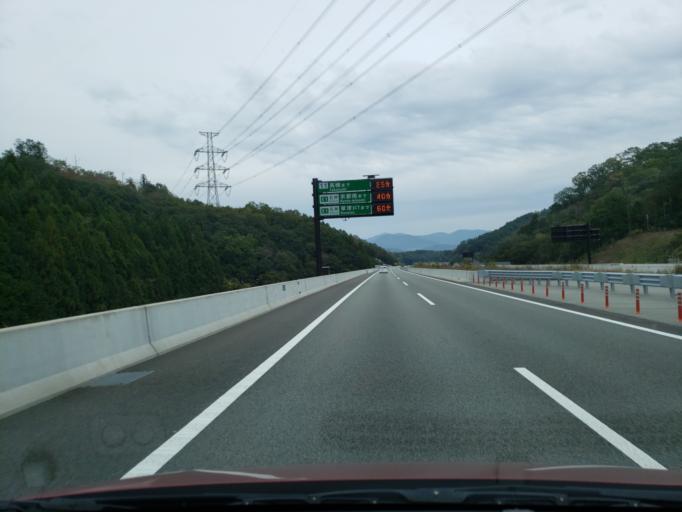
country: JP
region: Hyogo
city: Takarazuka
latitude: 34.8867
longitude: 135.3479
